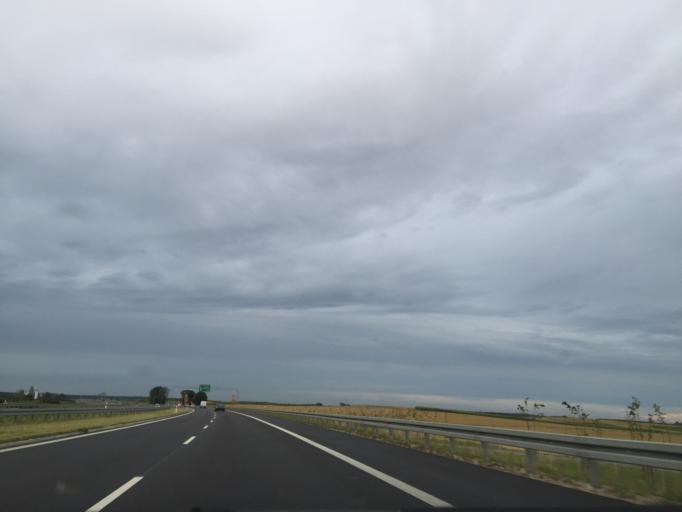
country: PL
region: Podlasie
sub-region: Powiat zambrowski
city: Rutki-Kossaki
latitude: 53.0861
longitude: 22.4829
